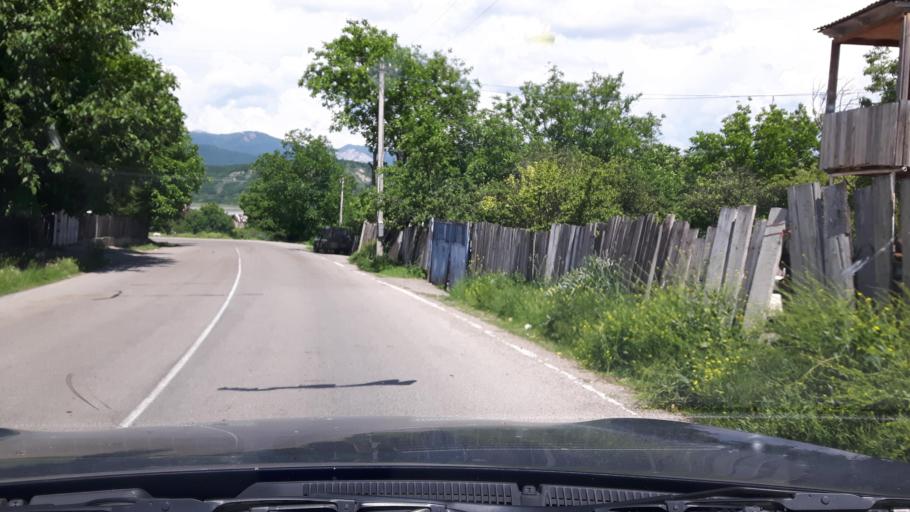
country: GE
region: Kakheti
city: Sagarejo
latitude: 41.7831
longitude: 45.1643
